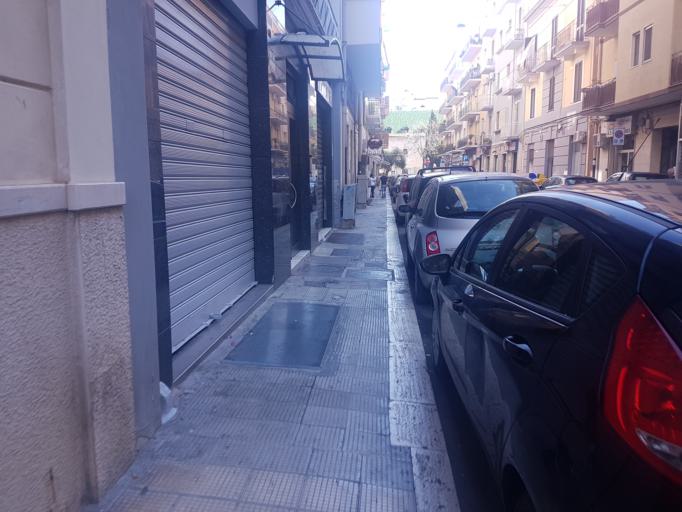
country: IT
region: Apulia
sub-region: Provincia di Bari
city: Bari
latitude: 41.1102
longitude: 16.8707
